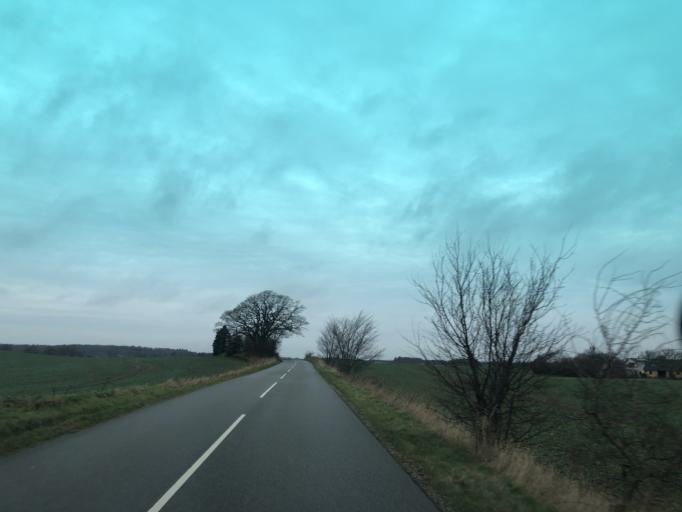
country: DK
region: Capital Region
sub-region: Allerod Kommune
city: Lynge
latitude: 55.8553
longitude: 12.2378
